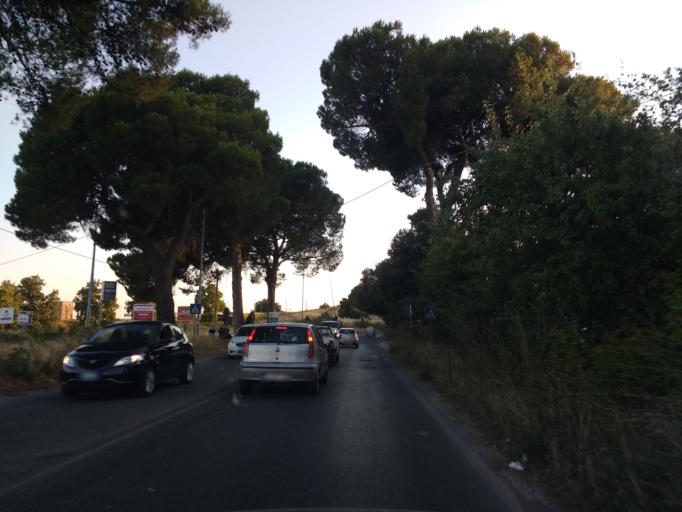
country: IT
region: Latium
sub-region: Citta metropolitana di Roma Capitale
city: Albuccione
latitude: 41.9513
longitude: 12.6864
